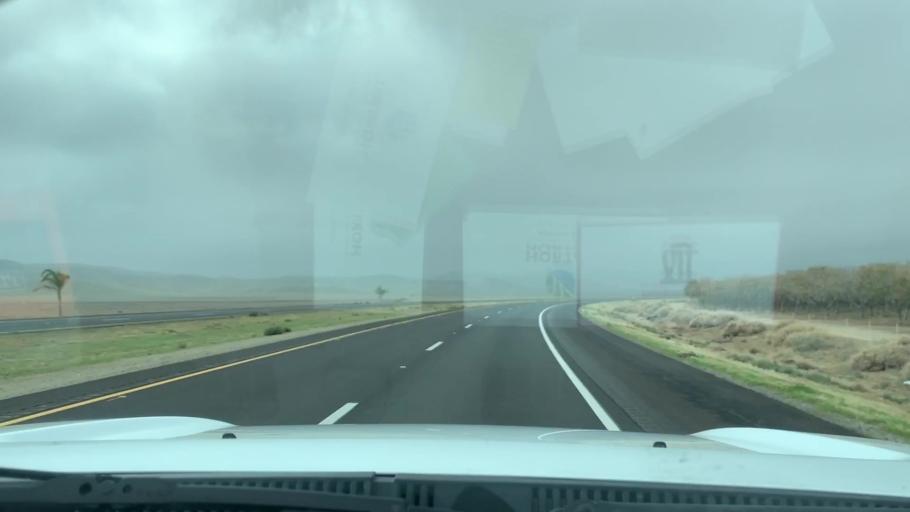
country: US
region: California
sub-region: Kern County
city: Lost Hills
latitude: 35.6145
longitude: -119.9626
